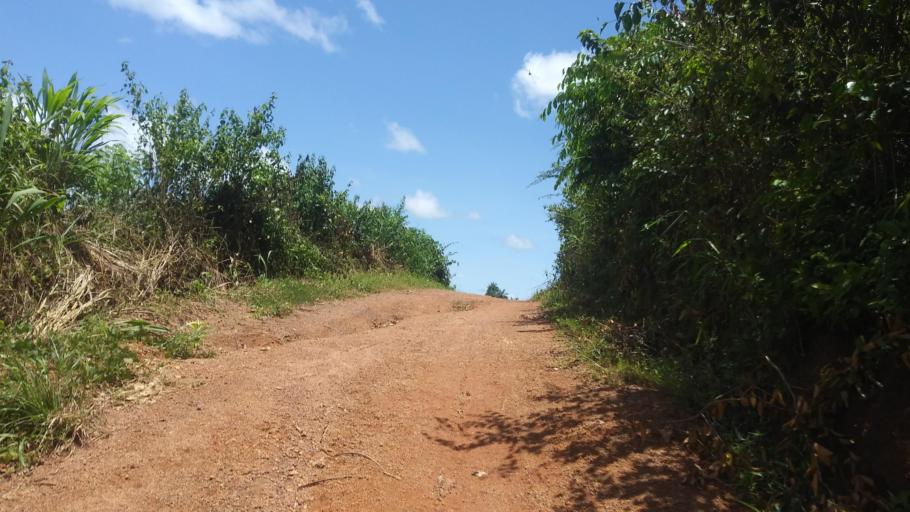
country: SL
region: Northern Province
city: Makeni
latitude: 8.8964
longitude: -11.9999
